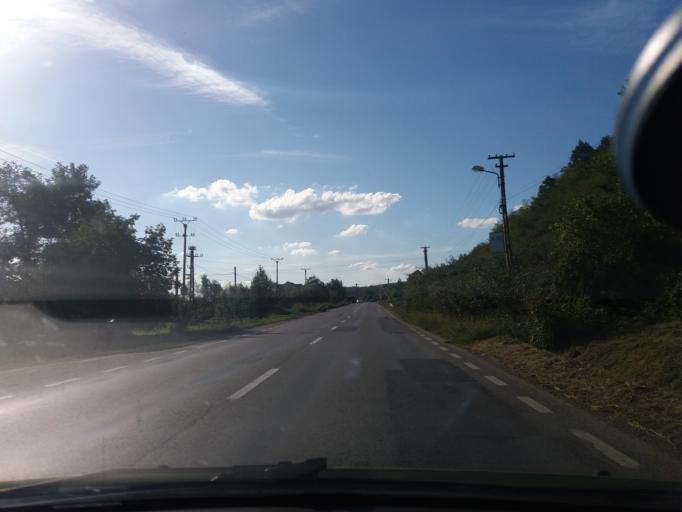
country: RO
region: Arad
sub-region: Oras Lipova
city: Radna
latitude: 46.1011
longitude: 21.6671
